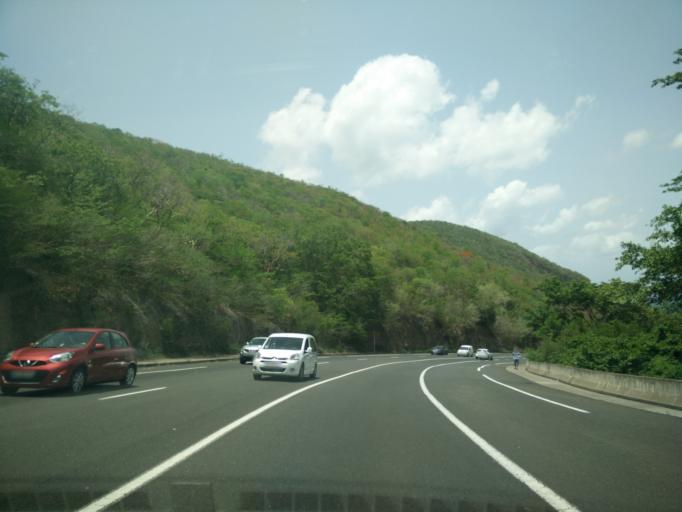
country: MQ
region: Martinique
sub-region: Martinique
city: Saint-Pierre
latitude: 14.6622
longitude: -61.1538
